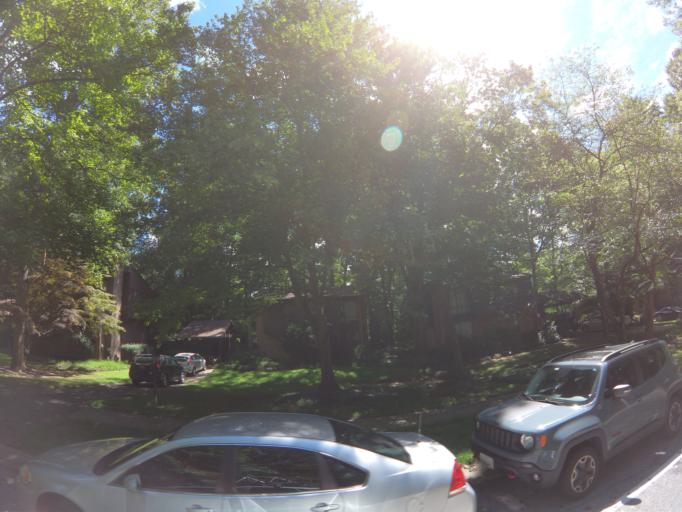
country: US
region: Maryland
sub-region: Howard County
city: Columbia
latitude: 39.2248
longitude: -76.8312
